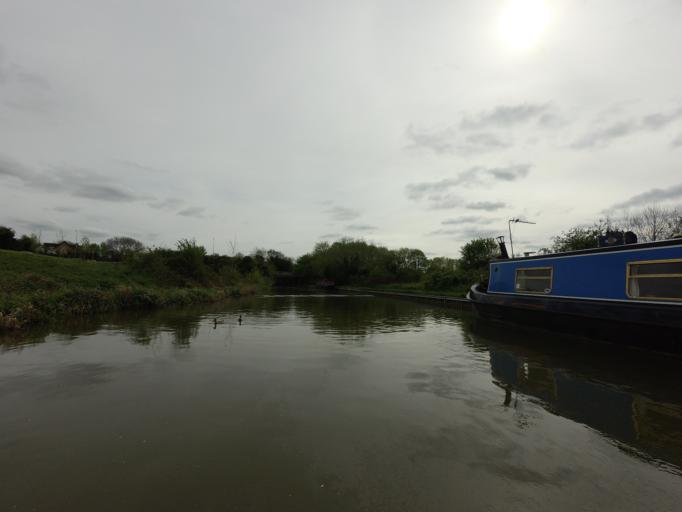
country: GB
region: England
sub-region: Milton Keynes
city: Bradwell
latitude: 52.0685
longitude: -0.7803
